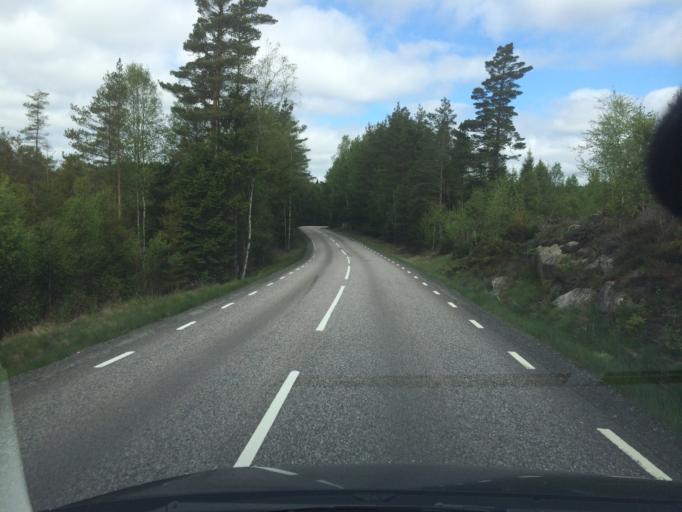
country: SE
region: Vaestra Goetaland
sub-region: Lerums Kommun
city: Stenkullen
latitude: 57.7139
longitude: 12.3472
